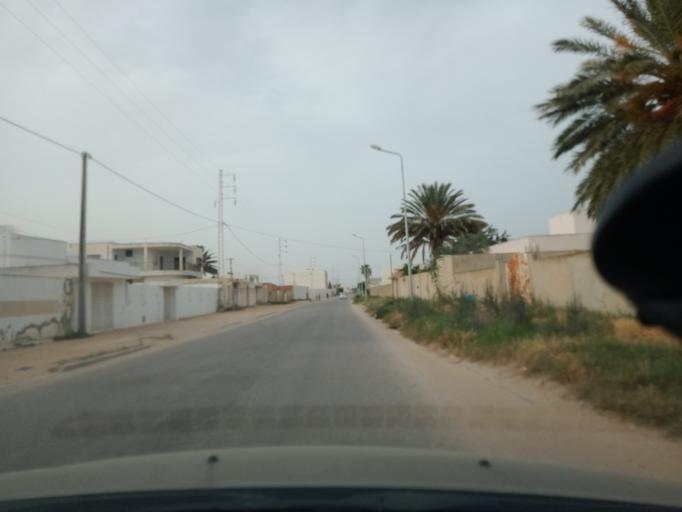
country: TN
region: Safaqis
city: Al Qarmadah
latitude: 34.7878
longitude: 10.7678
